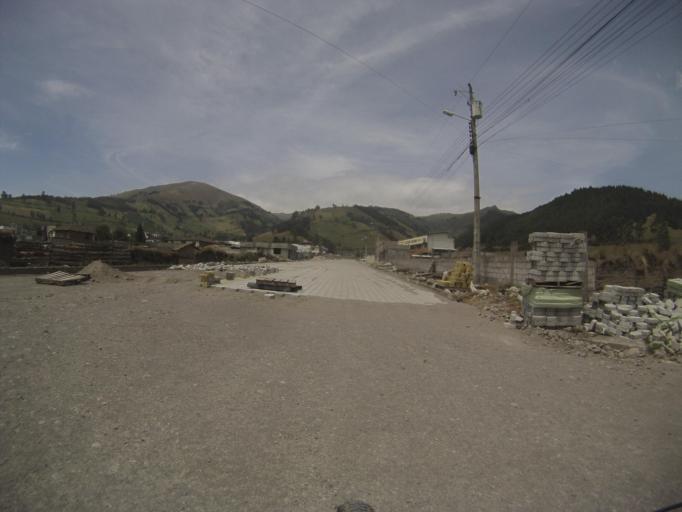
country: EC
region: Pichincha
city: Cayambe
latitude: 0.1576
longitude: -78.0667
